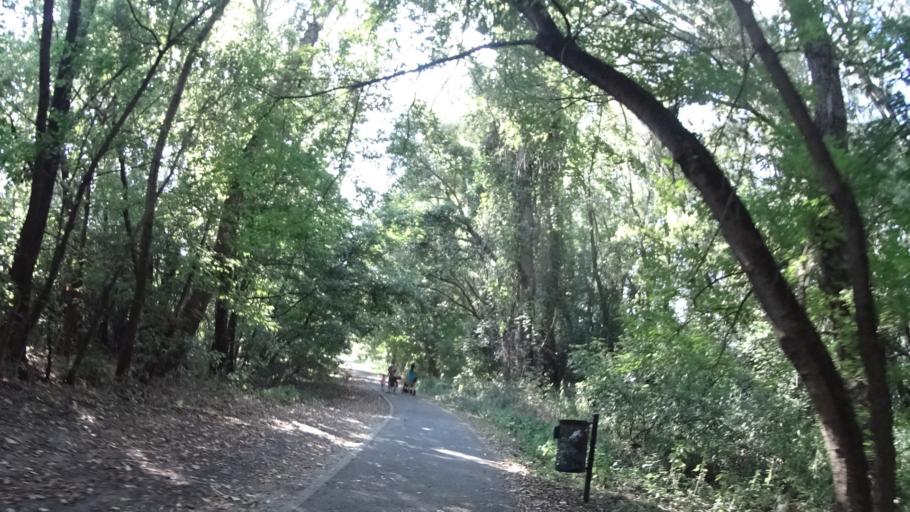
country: HU
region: Komarom-Esztergom
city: Esztergom
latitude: 47.8155
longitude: 18.7920
